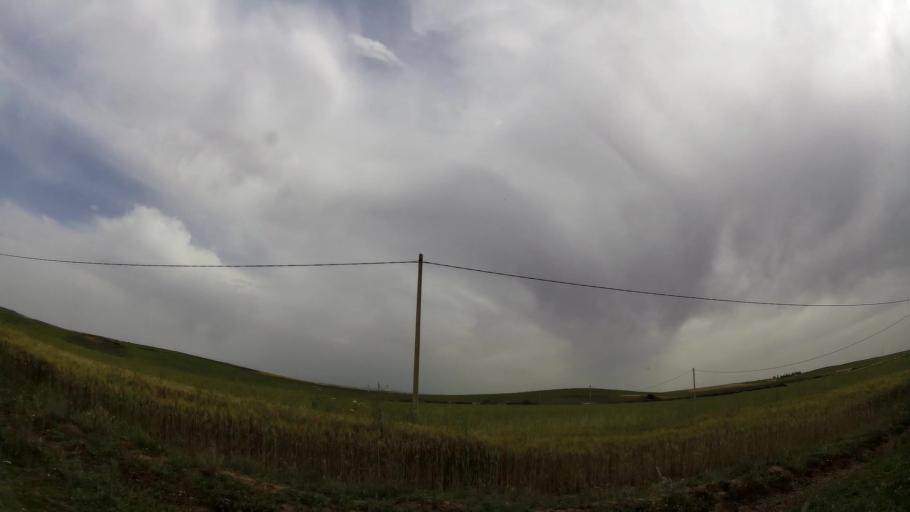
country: MA
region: Rabat-Sale-Zemmour-Zaer
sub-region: Khemisset
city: Tiflet
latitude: 33.7573
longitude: -6.2259
